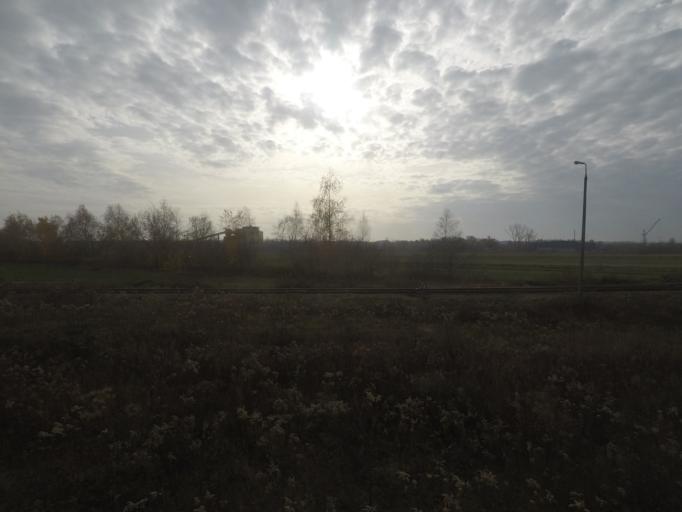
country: PL
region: Subcarpathian Voivodeship
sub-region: Powiat ropczycko-sedziszowski
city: Ostrow
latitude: 50.0795
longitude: 21.5995
